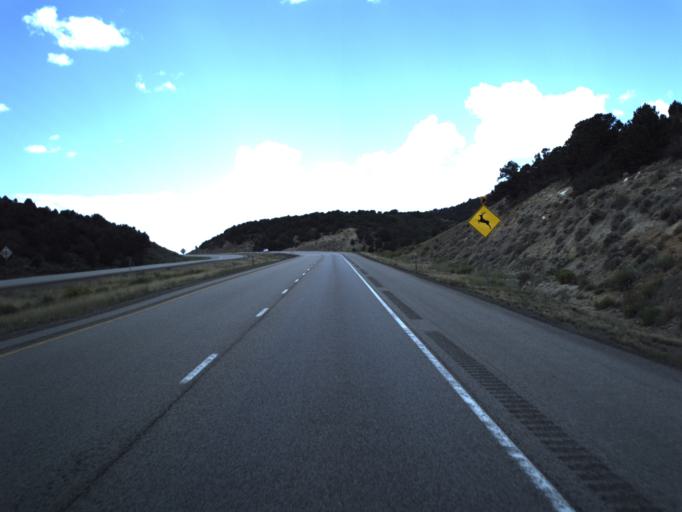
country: US
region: Utah
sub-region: Wayne County
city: Loa
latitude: 38.7752
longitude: -111.4764
